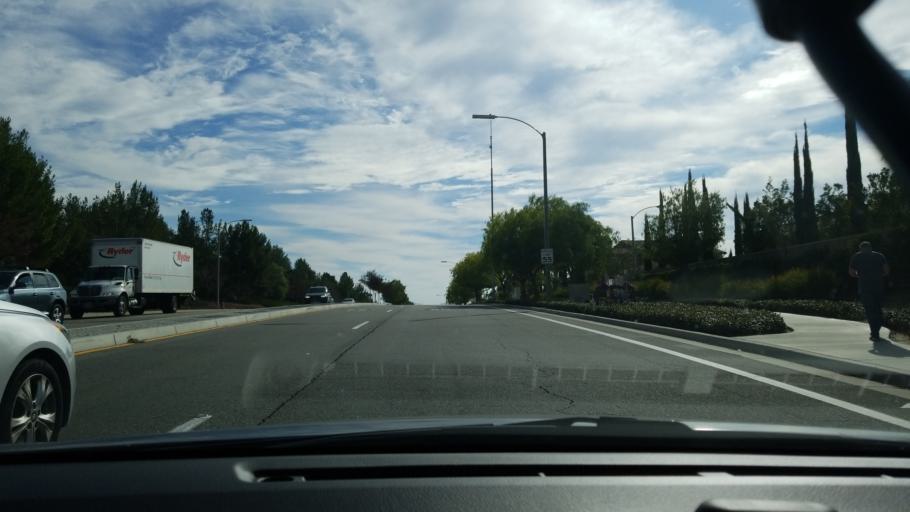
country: US
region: California
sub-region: Riverside County
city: Temecula
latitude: 33.5079
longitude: -117.0900
